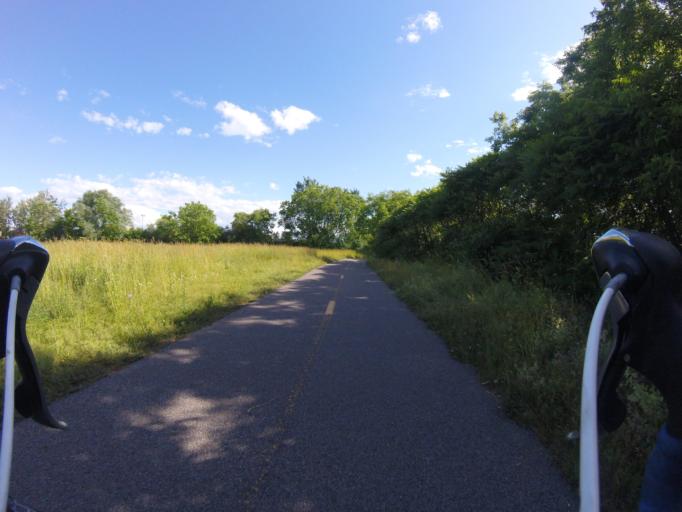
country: CA
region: Ontario
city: Ottawa
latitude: 45.4378
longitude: -75.7249
